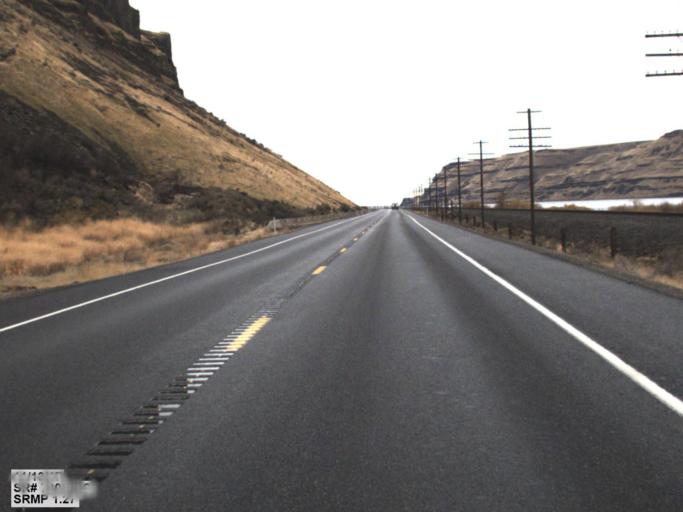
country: US
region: Washington
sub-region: Benton County
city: Finley
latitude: 46.0134
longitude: -118.9573
